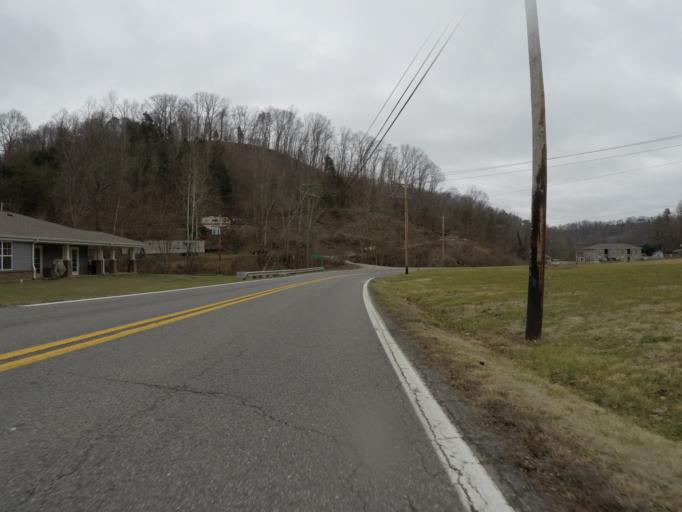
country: US
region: West Virginia
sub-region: Cabell County
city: Barboursville
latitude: 38.4390
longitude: -82.2918
